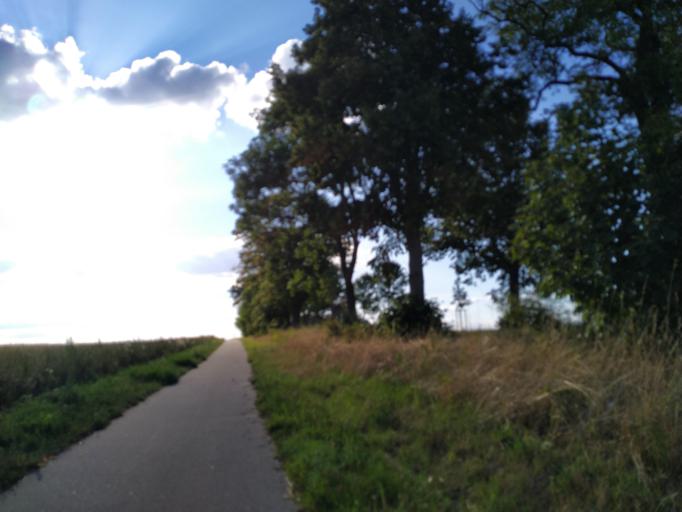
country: DE
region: Mecklenburg-Vorpommern
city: Klutz
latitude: 53.9613
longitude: 11.1875
